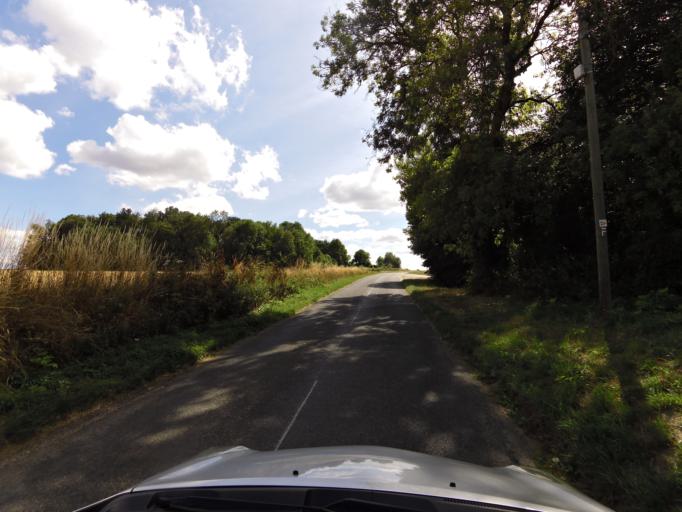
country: FR
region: Picardie
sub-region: Departement de l'Aisne
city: Bruyeres-et-Montberault
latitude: 49.5014
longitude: 3.6273
